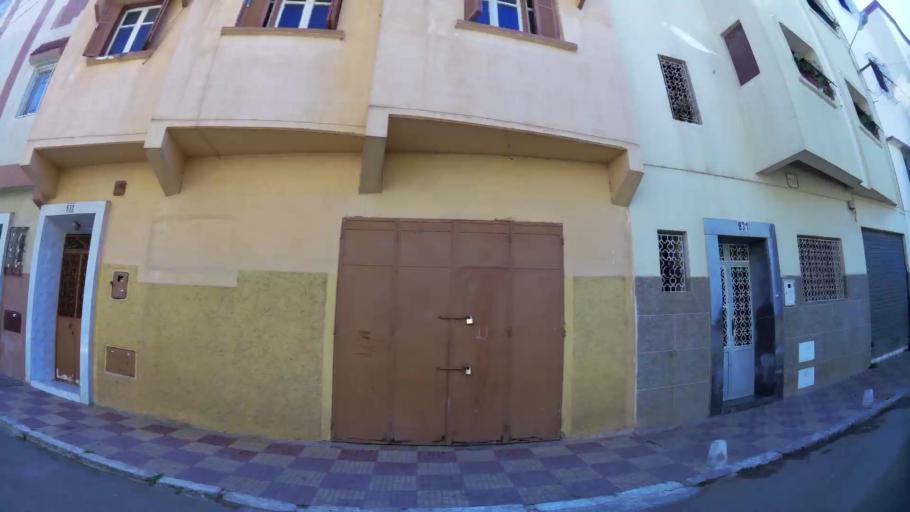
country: MA
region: Meknes-Tafilalet
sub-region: Meknes
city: Meknes
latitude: 33.8797
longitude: -5.5598
